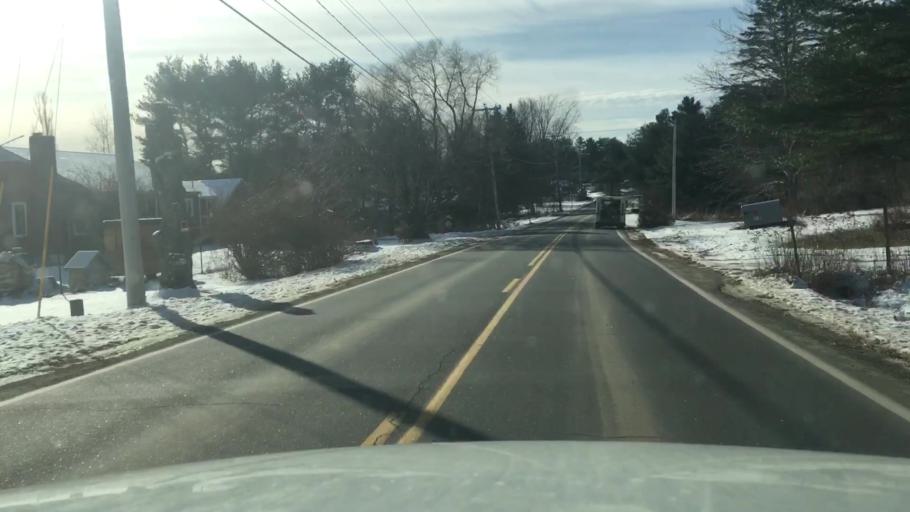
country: US
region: Maine
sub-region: Lincoln County
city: Wiscasset
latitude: 43.9639
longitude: -69.6992
